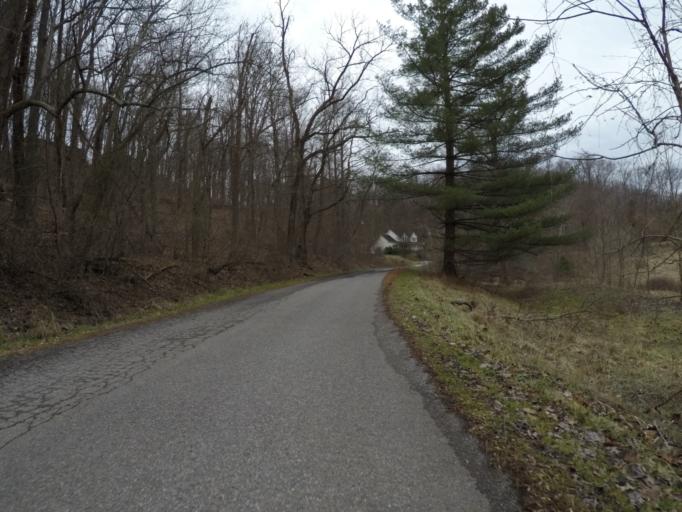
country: US
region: Ohio
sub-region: Lawrence County
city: Burlington
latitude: 38.3810
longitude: -82.5107
